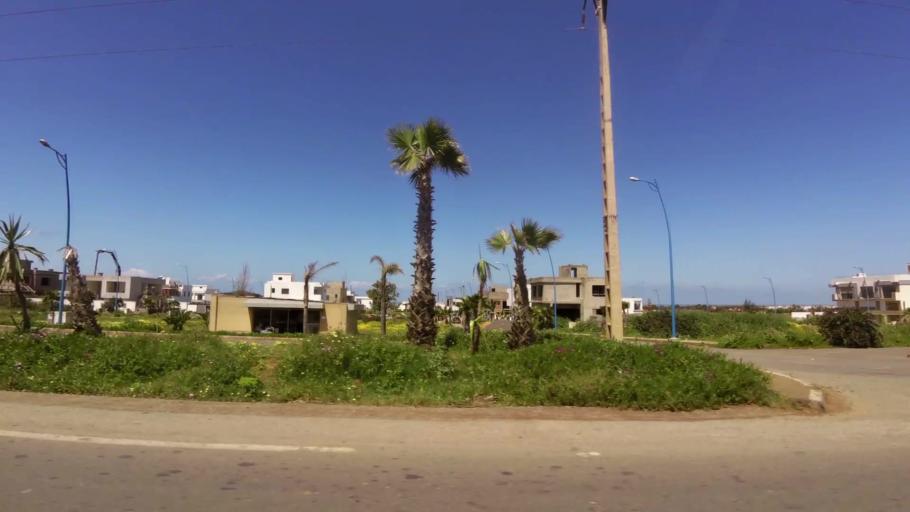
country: MA
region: Grand Casablanca
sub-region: Nouaceur
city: Dar Bouazza
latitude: 33.5328
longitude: -7.7688
